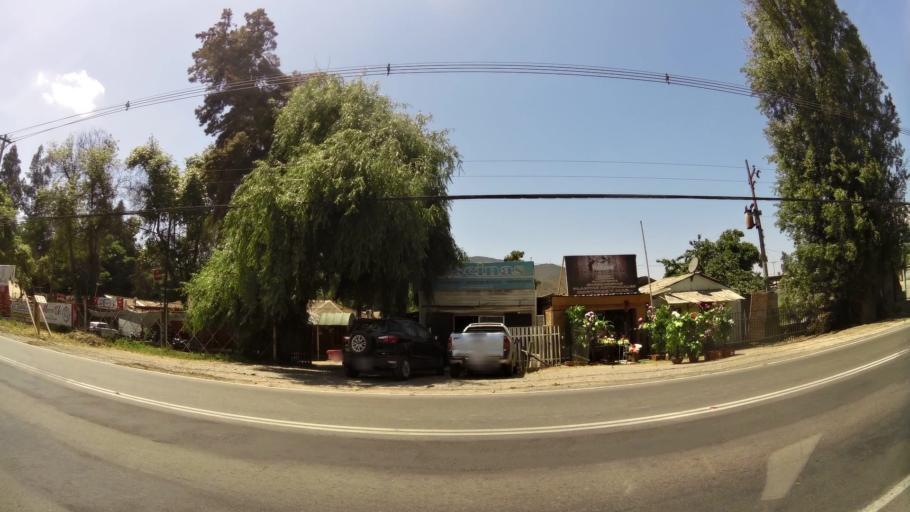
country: CL
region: Santiago Metropolitan
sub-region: Provincia de Maipo
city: San Bernardo
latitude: -33.5895
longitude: -70.7804
